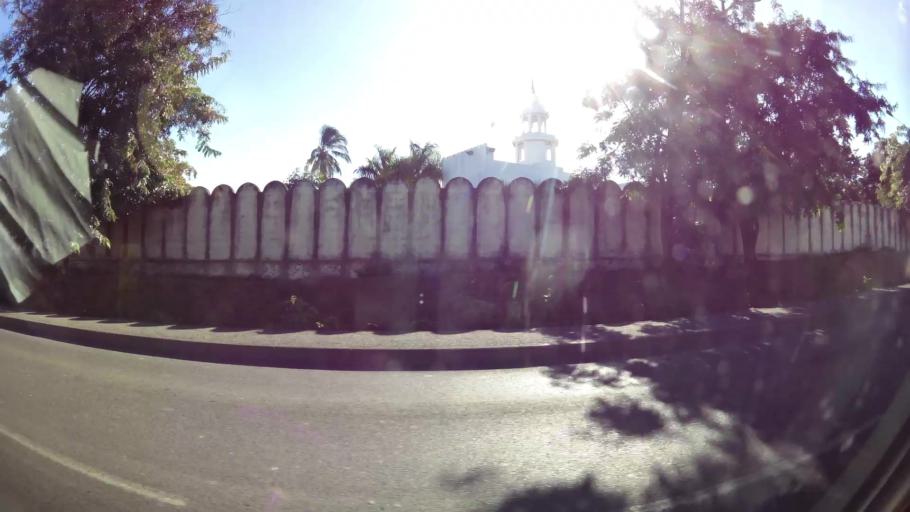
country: YT
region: Mamoudzou
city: Mamoudzou
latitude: -12.7645
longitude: 45.2254
